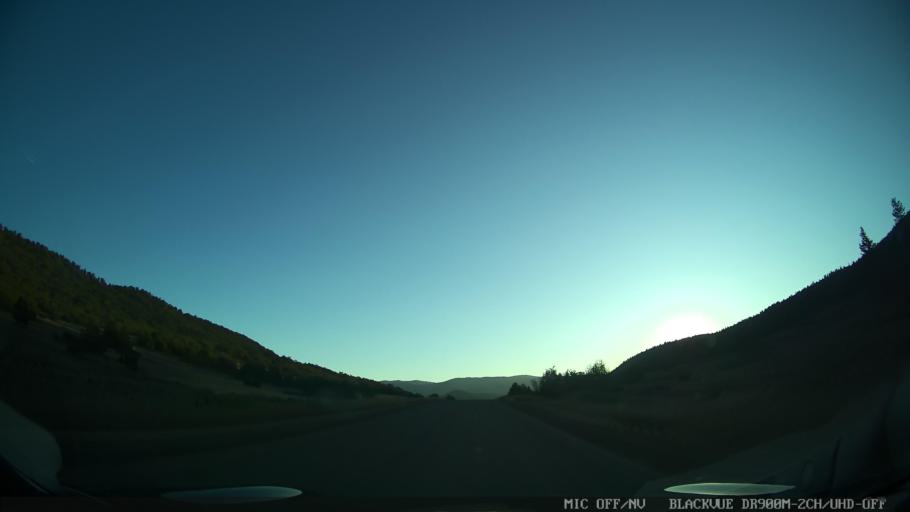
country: US
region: Colorado
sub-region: Grand County
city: Kremmling
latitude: 39.9139
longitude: -106.5597
